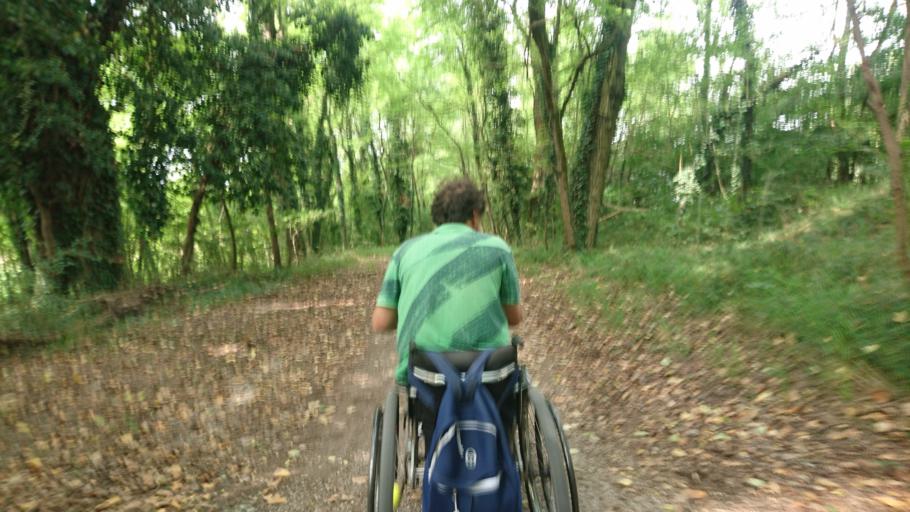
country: IT
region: Veneto
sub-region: Provincia di Padova
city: Piazzola sul Brenta
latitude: 45.5701
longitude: 11.7648
